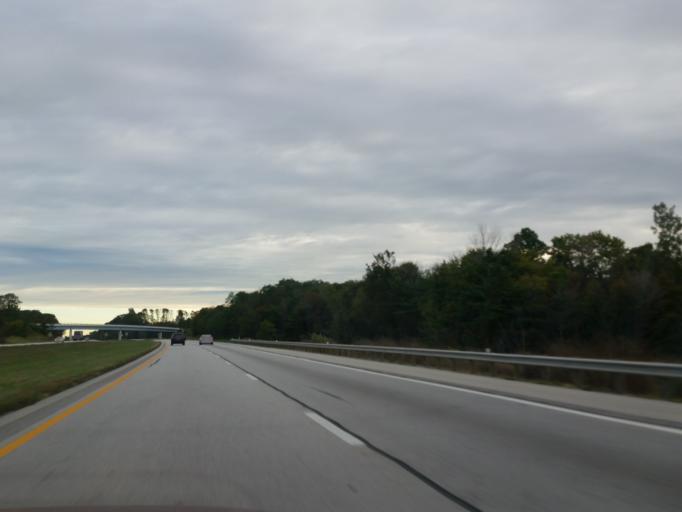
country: US
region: Ohio
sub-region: Ashtabula County
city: North Kingsville
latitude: 41.8506
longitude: -80.7016
